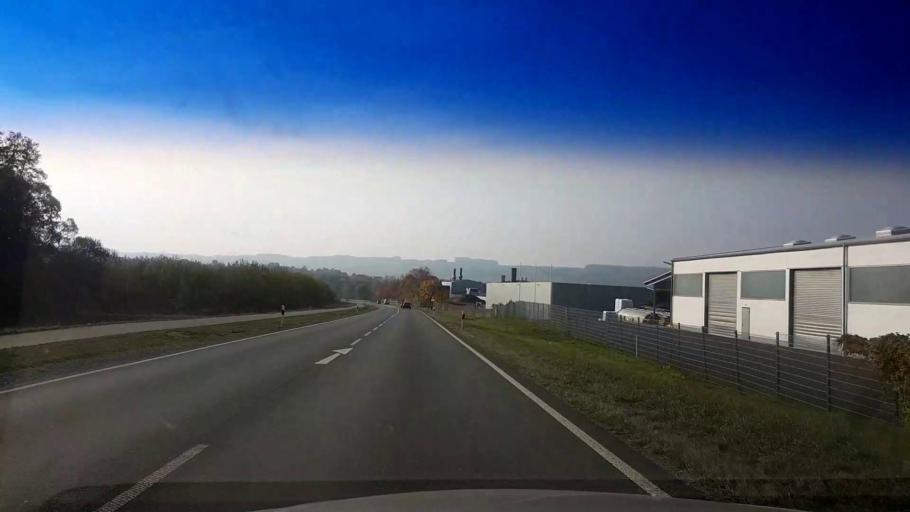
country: DE
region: Bavaria
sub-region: Upper Franconia
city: Himmelkron
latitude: 50.0699
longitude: 11.6067
